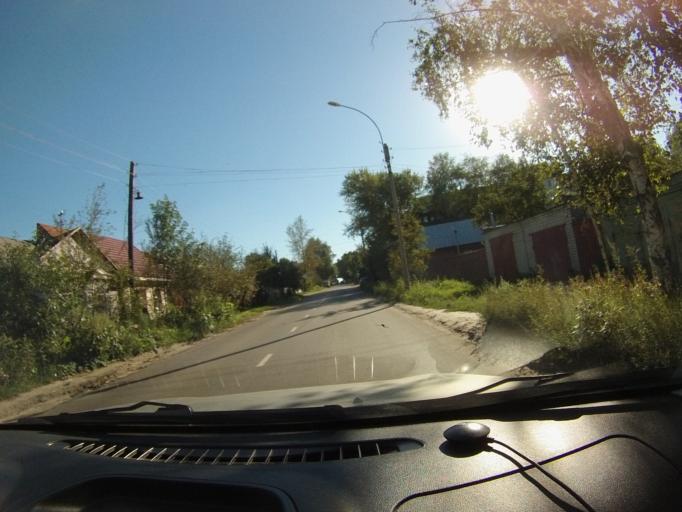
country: RU
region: Tambov
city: Tambov
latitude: 52.7505
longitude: 41.4237
